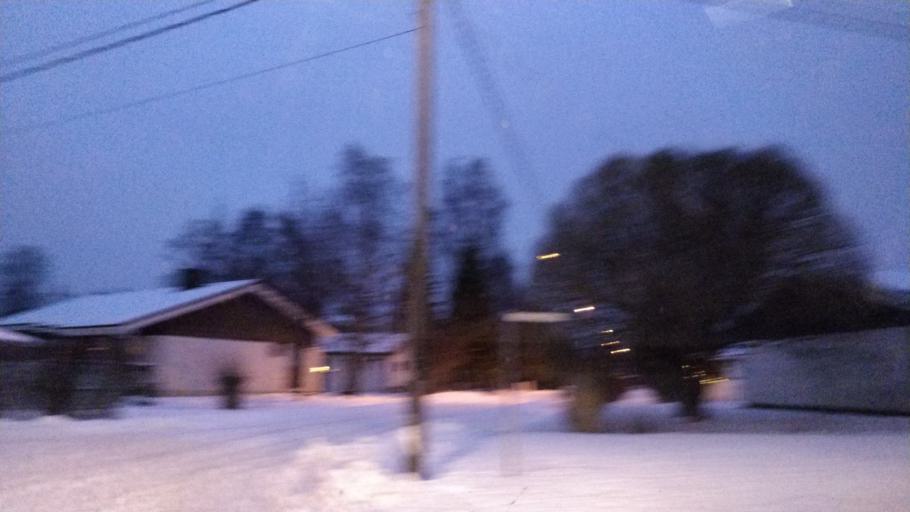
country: FI
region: Lapland
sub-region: Kemi-Tornio
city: Kemi
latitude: 65.7451
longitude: 24.5757
